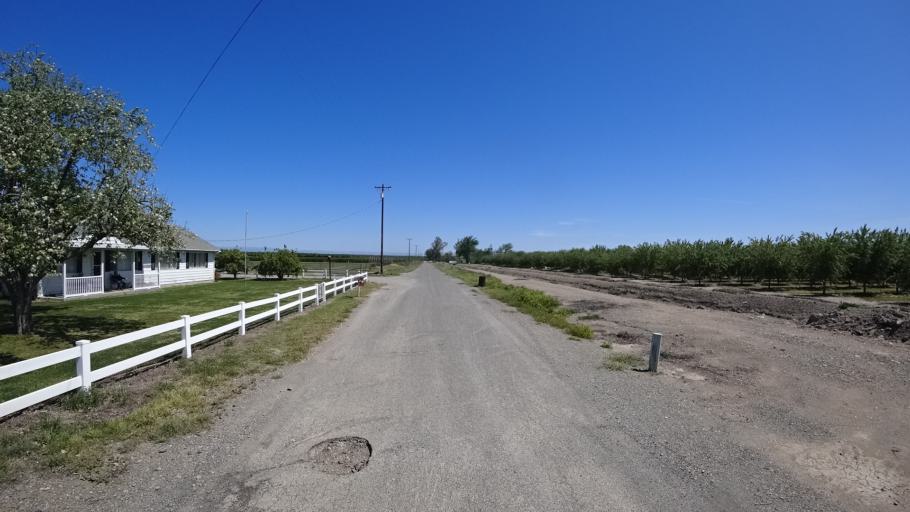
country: US
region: California
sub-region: Glenn County
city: Hamilton City
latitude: 39.7286
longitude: -122.0950
